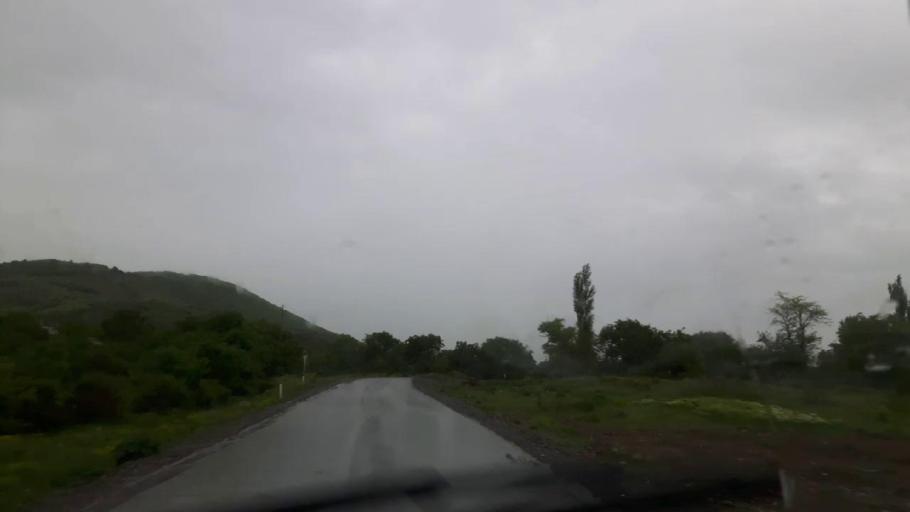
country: GE
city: Agara
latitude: 41.9814
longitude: 43.9424
